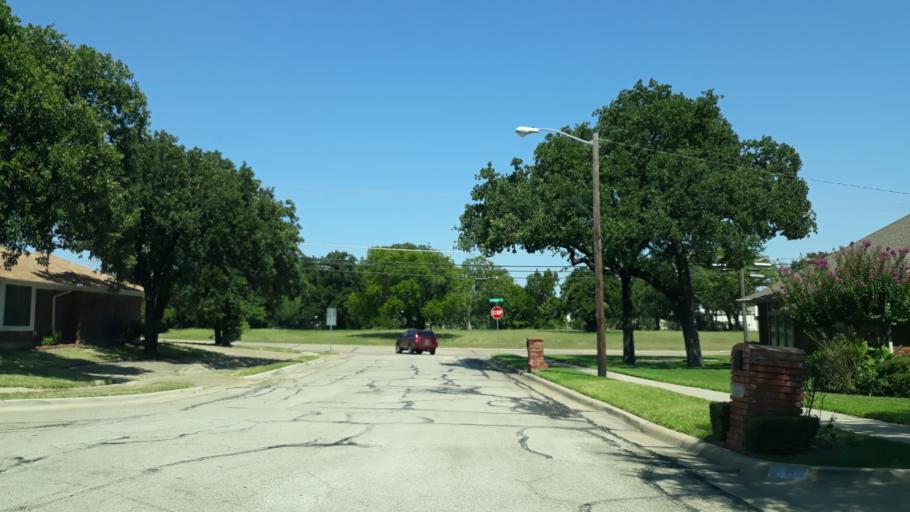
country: US
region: Texas
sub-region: Dallas County
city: Irving
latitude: 32.8226
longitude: -97.0050
